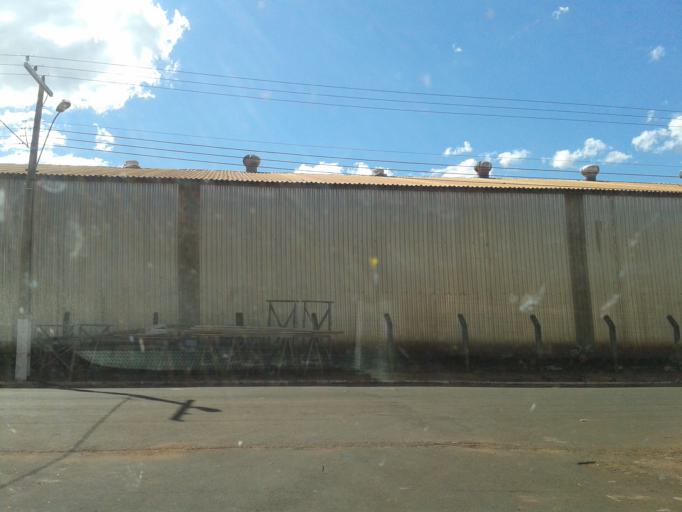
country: BR
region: Minas Gerais
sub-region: Santa Vitoria
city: Santa Vitoria
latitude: -18.6927
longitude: -49.9492
